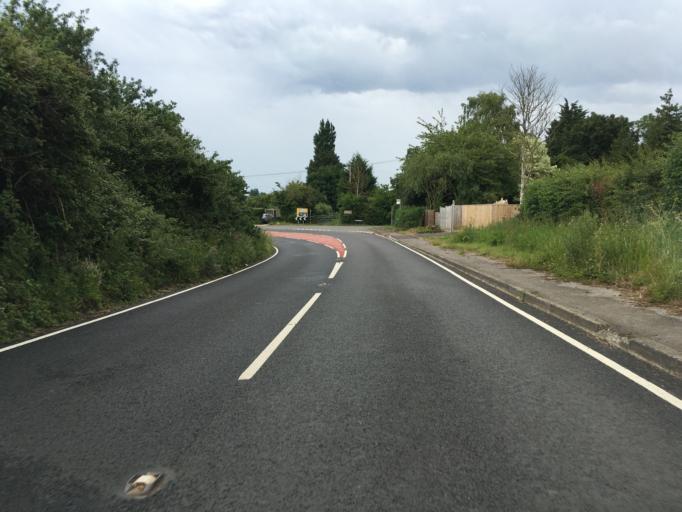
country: GB
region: England
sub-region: Gloucestershire
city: Stonehouse
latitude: 51.7801
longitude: -2.2877
